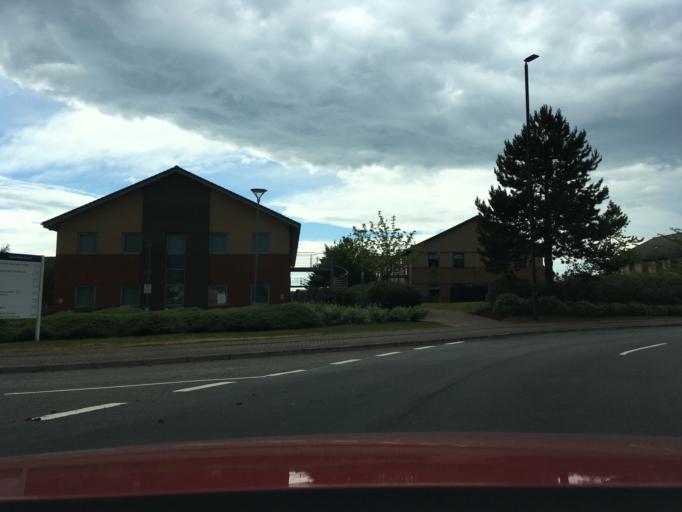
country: GB
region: England
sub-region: Gloucestershire
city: Barnwood
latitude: 51.8463
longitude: -2.1764
